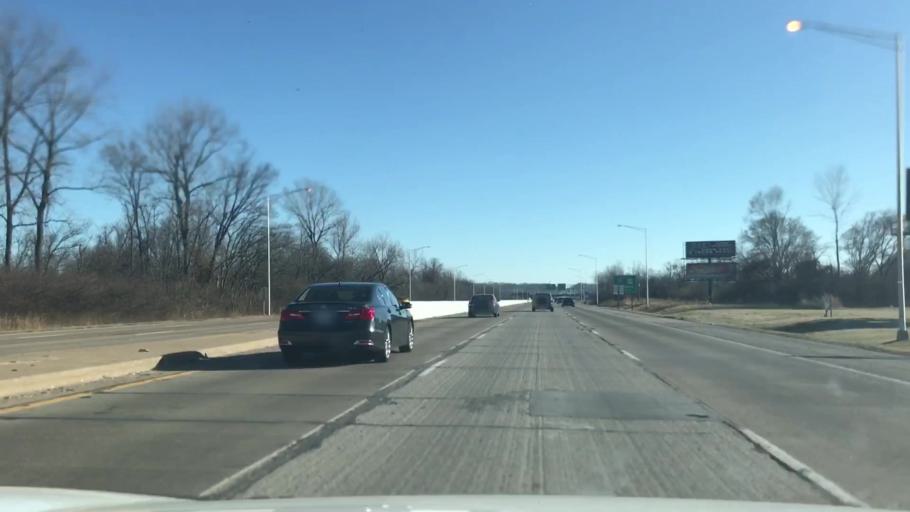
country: US
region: Illinois
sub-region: Saint Clair County
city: Alorton
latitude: 38.5897
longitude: -90.1161
